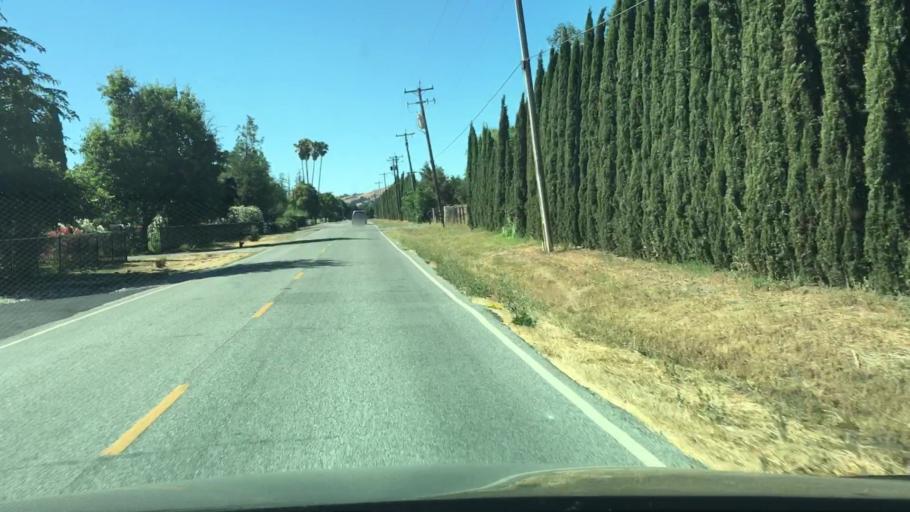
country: US
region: California
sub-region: Santa Clara County
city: San Martin
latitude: 37.1129
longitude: -121.5915
